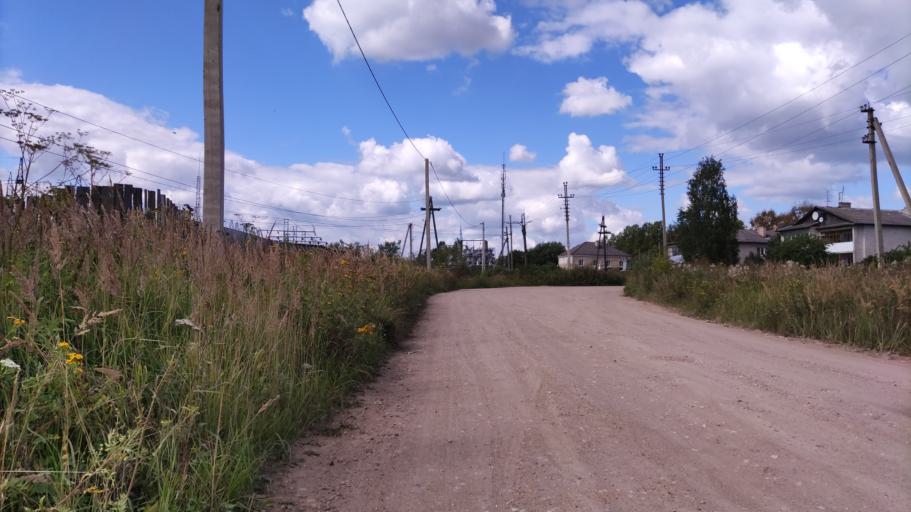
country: RU
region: Tverskaya
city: Rzhev
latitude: 56.2374
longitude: 34.3233
